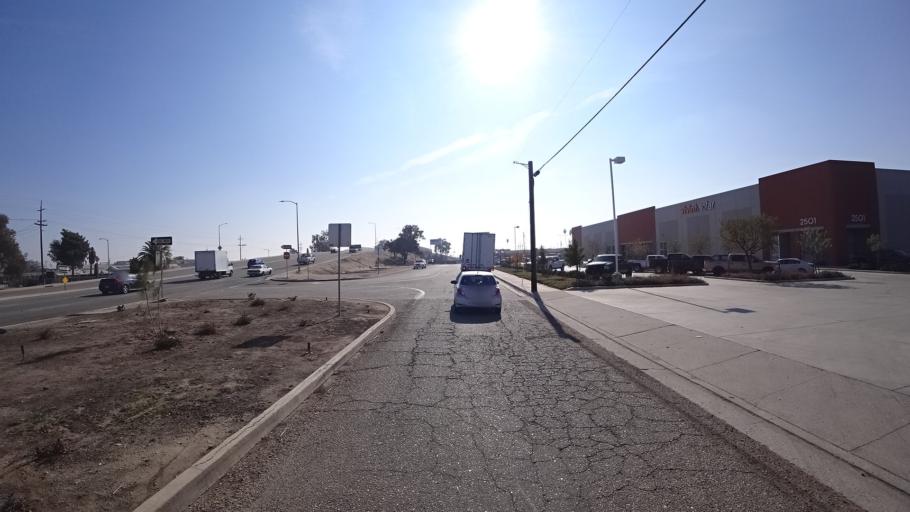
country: US
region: California
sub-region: Kern County
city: Bakersfield
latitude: 35.3823
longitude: -119.0030
